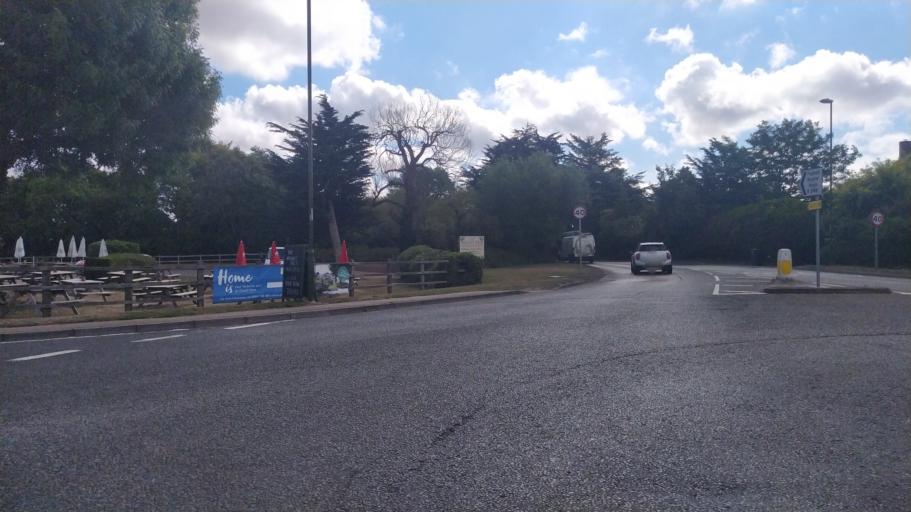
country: GB
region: England
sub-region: West Sussex
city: Chichester
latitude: 50.8151
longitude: -0.7514
